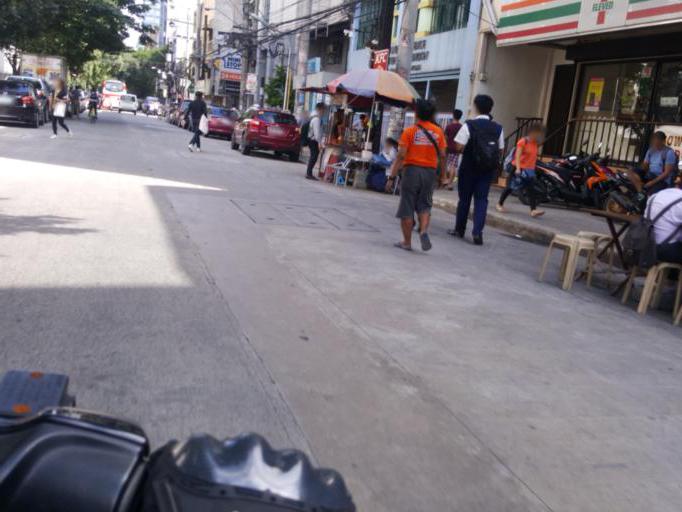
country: PH
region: Metro Manila
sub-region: City of Manila
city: Manila
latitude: 14.6084
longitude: 120.9879
